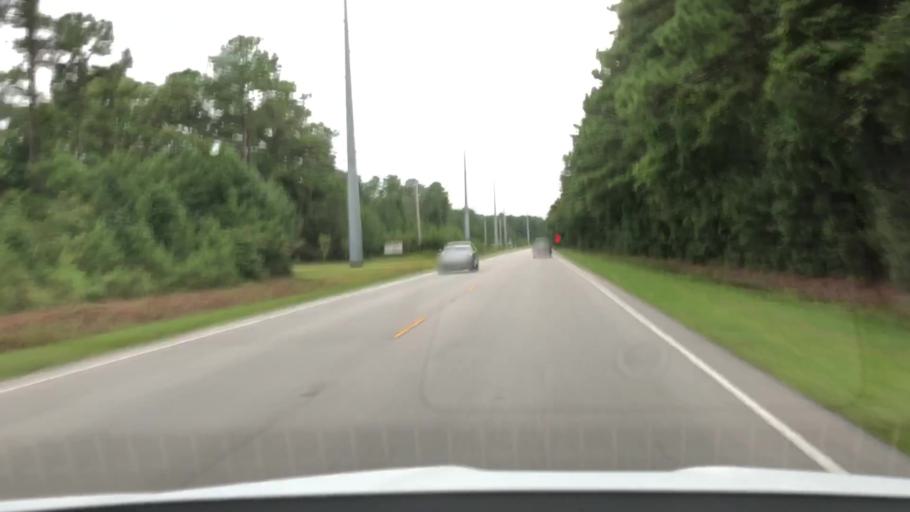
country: US
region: North Carolina
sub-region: Carteret County
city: Cape Carteret
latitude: 34.7443
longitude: -77.0887
